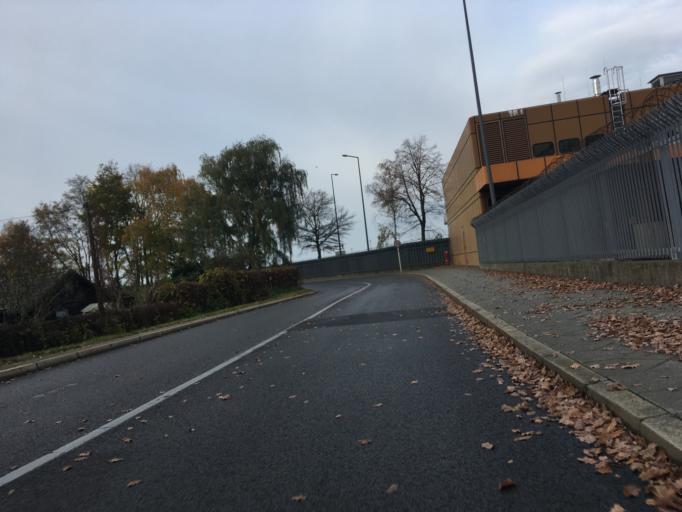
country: DE
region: Berlin
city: Charlottenburg-Nord
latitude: 52.5498
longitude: 13.2907
